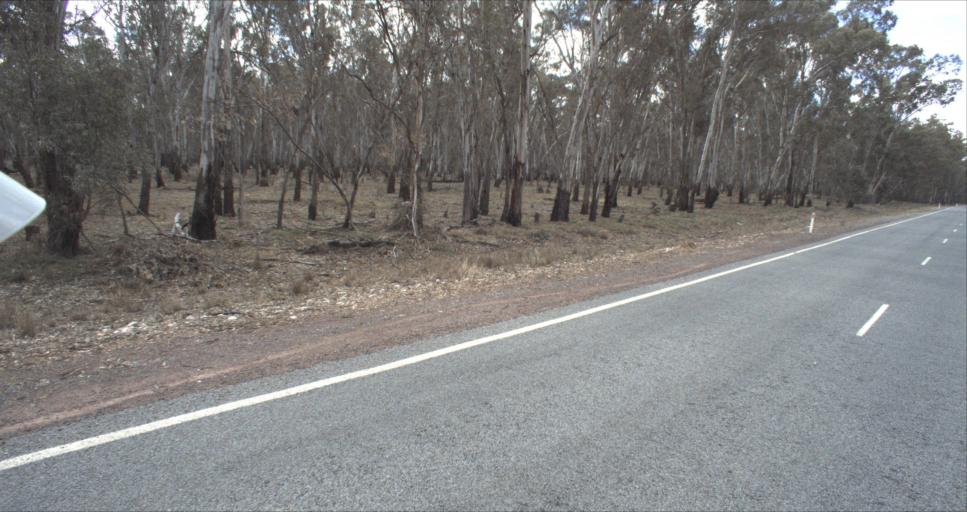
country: AU
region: New South Wales
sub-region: Leeton
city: Leeton
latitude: -34.6273
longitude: 146.3783
